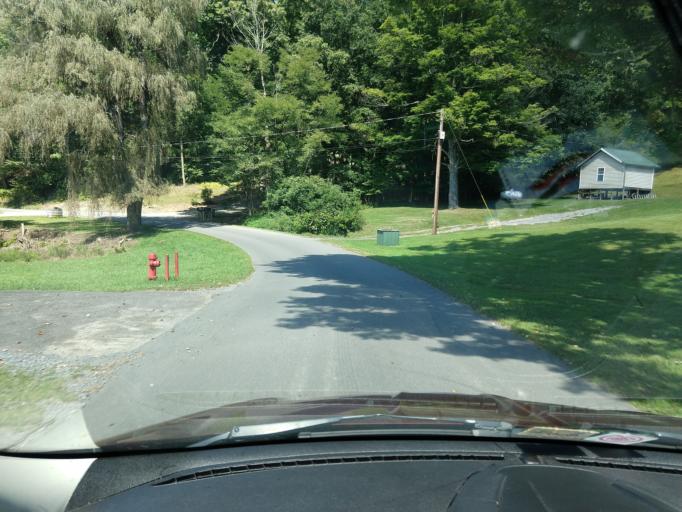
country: US
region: West Virginia
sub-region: Nicholas County
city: Craigsville
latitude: 38.2822
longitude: -80.7353
